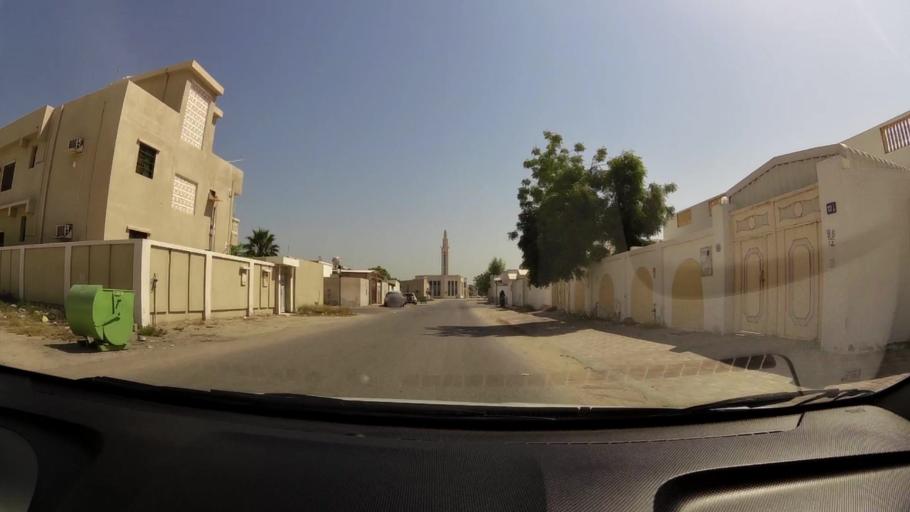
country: AE
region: Umm al Qaywayn
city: Umm al Qaywayn
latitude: 25.5802
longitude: 55.5583
